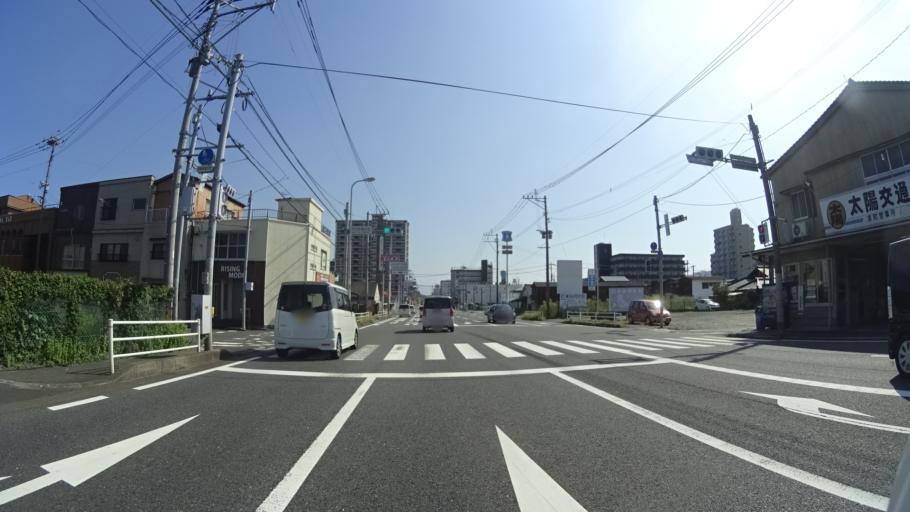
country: JP
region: Fukuoka
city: Kanda
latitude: 33.7840
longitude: 130.9824
